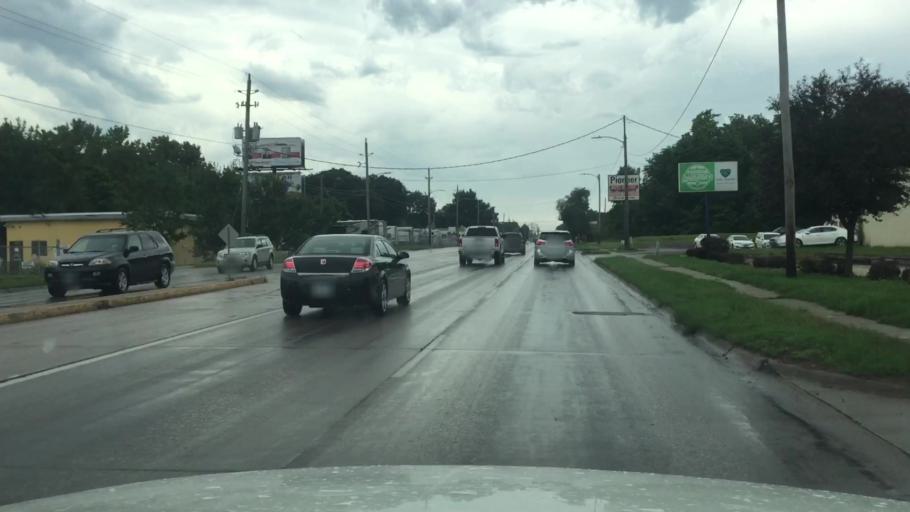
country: US
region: Iowa
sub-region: Polk County
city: Des Moines
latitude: 41.5682
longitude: -93.5970
